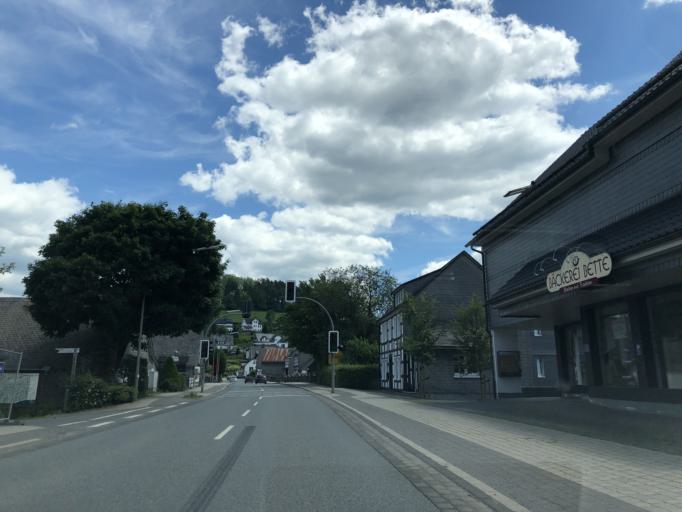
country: DE
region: North Rhine-Westphalia
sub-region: Regierungsbezirk Arnsberg
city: Schmallenberg
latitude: 51.1363
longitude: 8.2581
